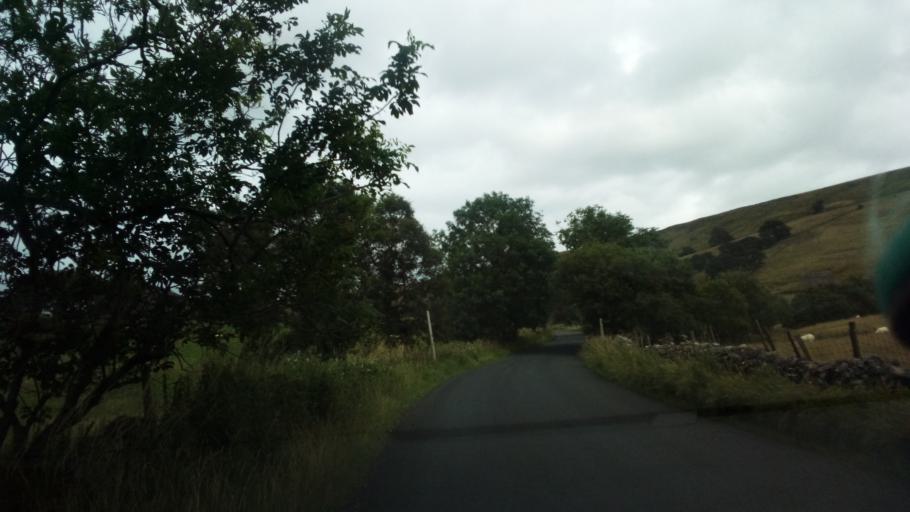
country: GB
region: England
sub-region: Cumbria
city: Kirkby Stephen
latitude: 54.4206
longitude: -2.3349
